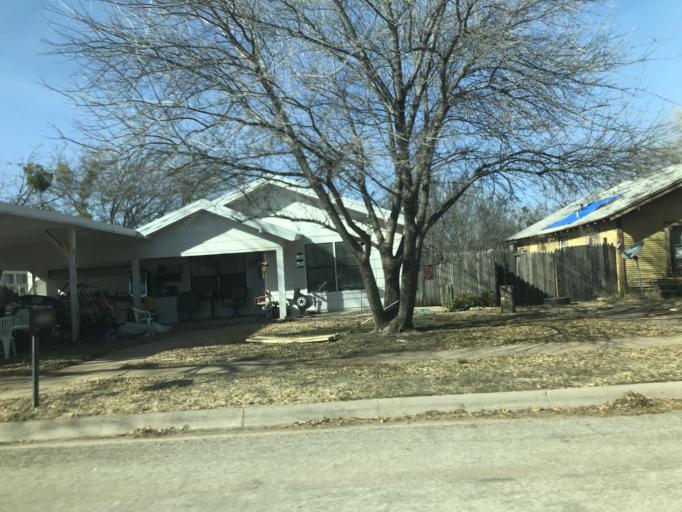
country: US
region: Texas
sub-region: Taylor County
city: Abilene
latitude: 32.4734
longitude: -99.7417
